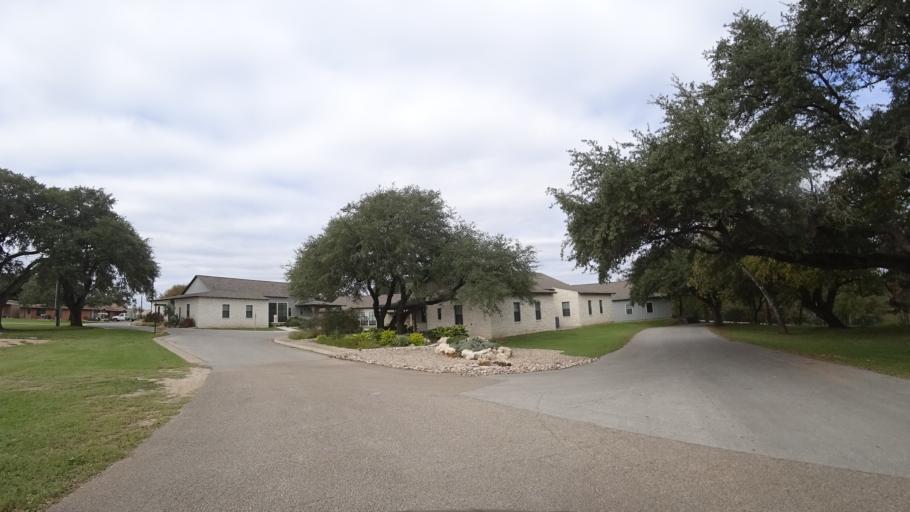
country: US
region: Texas
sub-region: Travis County
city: Manchaca
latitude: 30.1380
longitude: -97.8525
